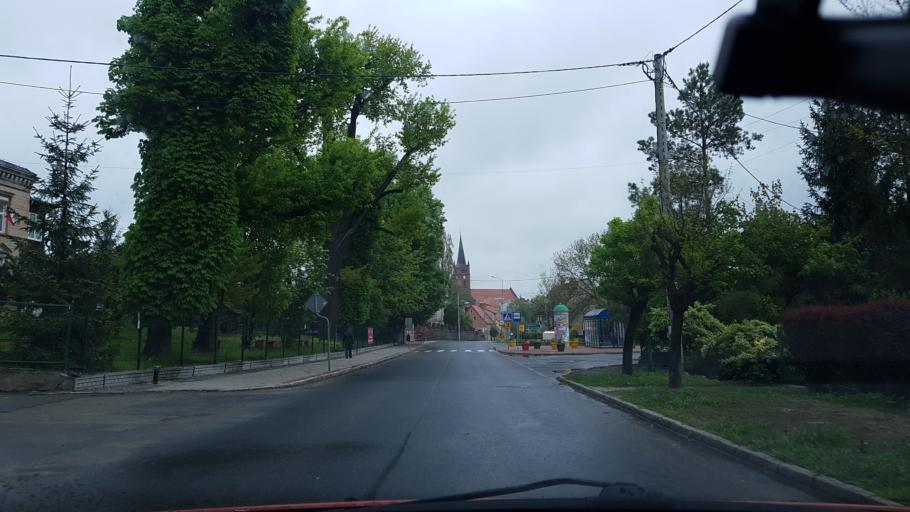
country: PL
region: Lower Silesian Voivodeship
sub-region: Powiat dzierzoniowski
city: Niemcza
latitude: 50.7131
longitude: 16.8330
